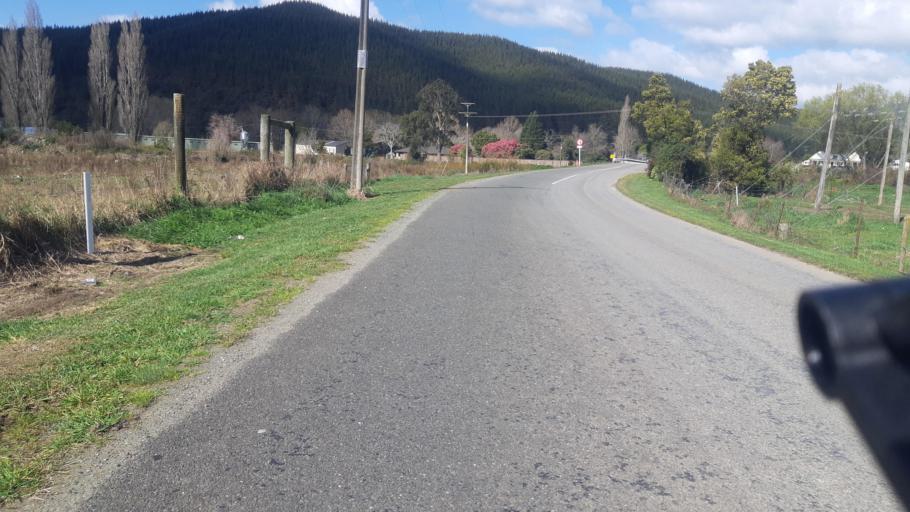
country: NZ
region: Tasman
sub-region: Tasman District
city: Wakefield
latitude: -41.4473
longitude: 172.9660
